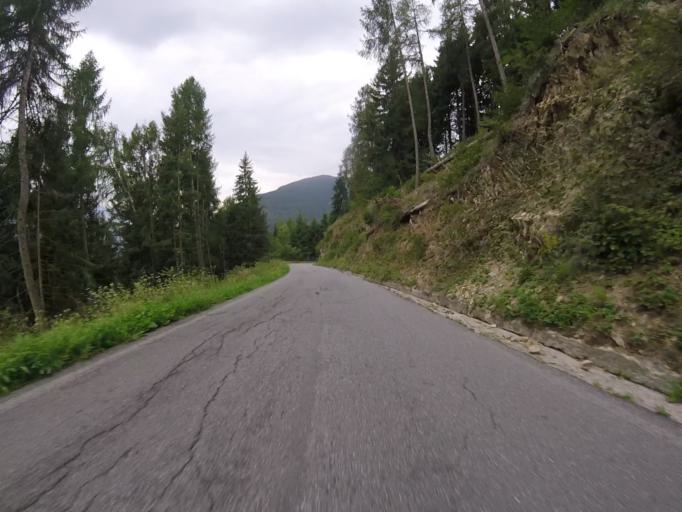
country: IT
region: Lombardy
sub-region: Provincia di Brescia
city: Monno
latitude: 46.2181
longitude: 10.3369
